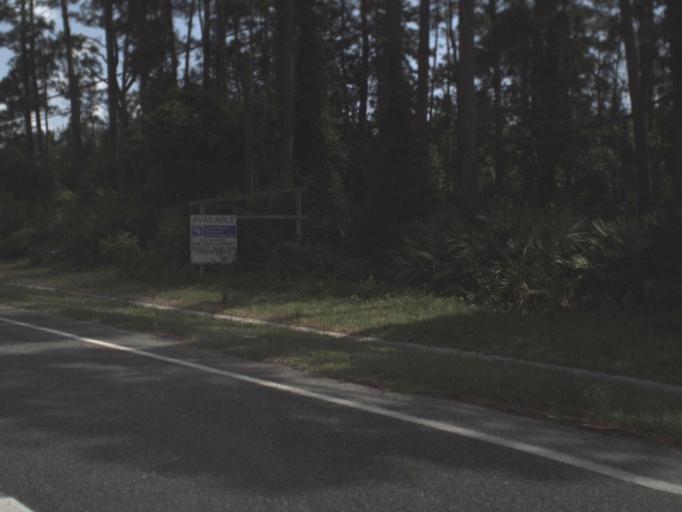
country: US
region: Florida
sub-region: Saint Johns County
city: Saint Augustine Shores
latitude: 29.8046
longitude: -81.3209
